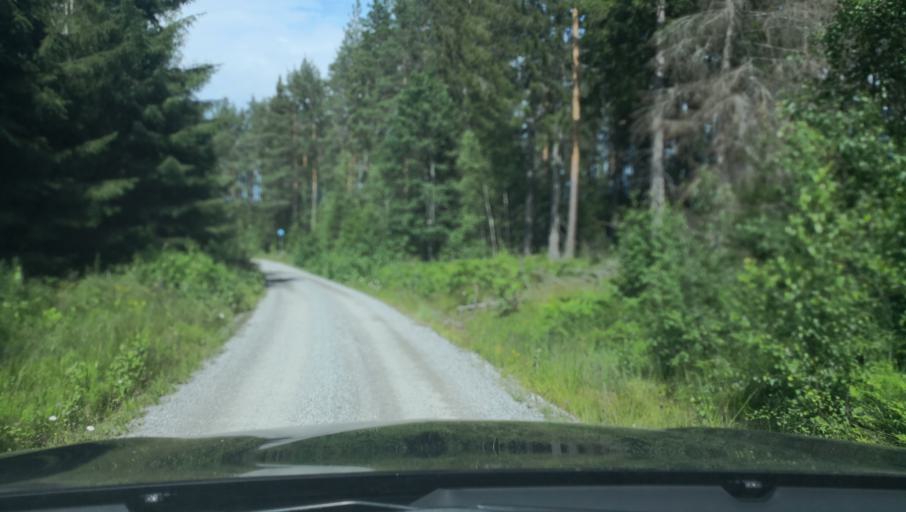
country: SE
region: Vaestmanland
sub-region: Surahammars Kommun
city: Ramnas
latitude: 59.9371
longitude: 16.1941
